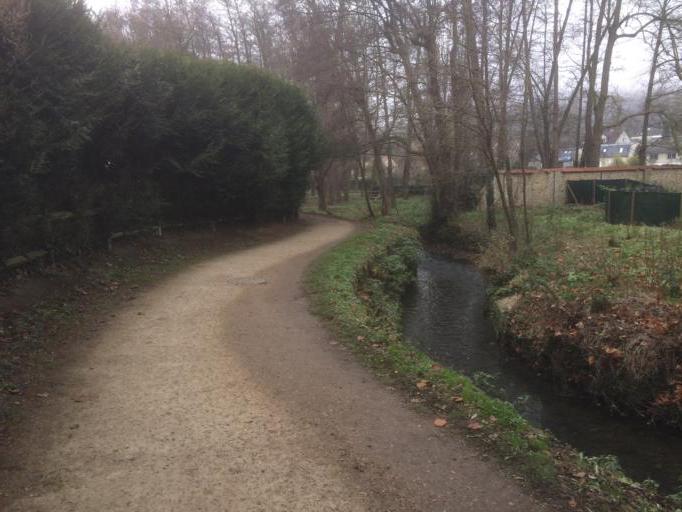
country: FR
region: Ile-de-France
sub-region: Departement de l'Essonne
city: Igny
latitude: 48.7462
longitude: 2.2291
